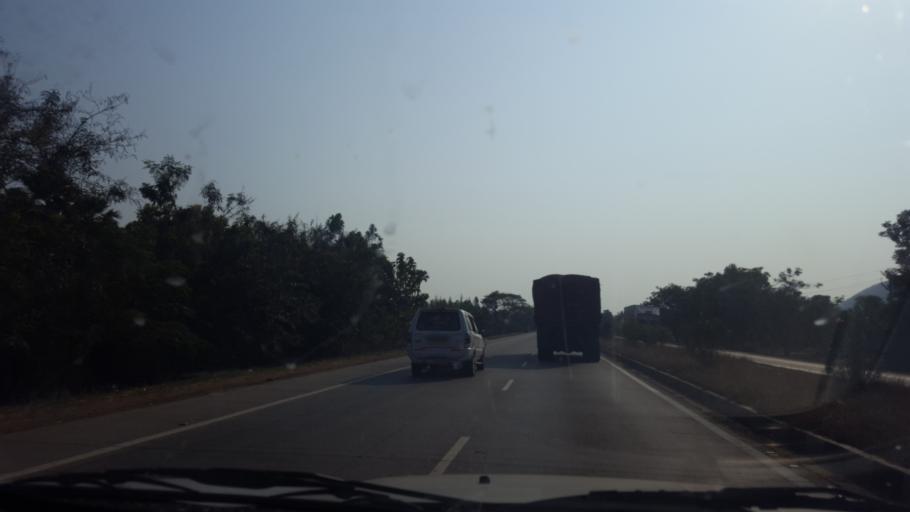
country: IN
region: Andhra Pradesh
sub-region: Vishakhapatnam
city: Elamanchili
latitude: 17.5536
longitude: 82.8437
